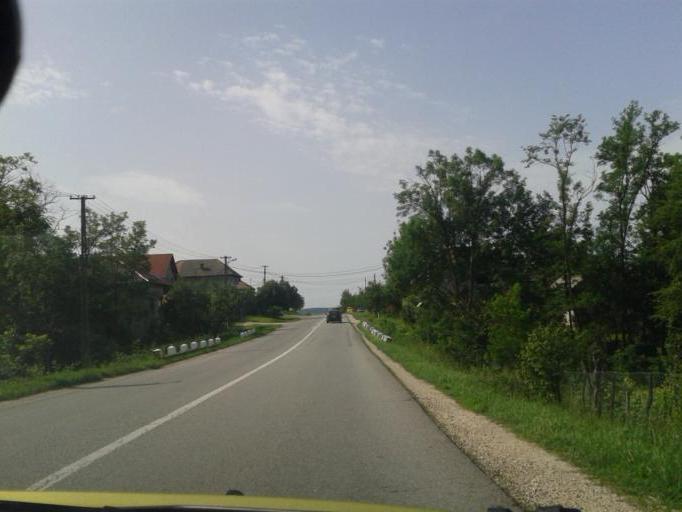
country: RO
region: Valcea
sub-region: Comuna Barbatesti
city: Bodesti
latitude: 45.1195
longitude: 24.1160
